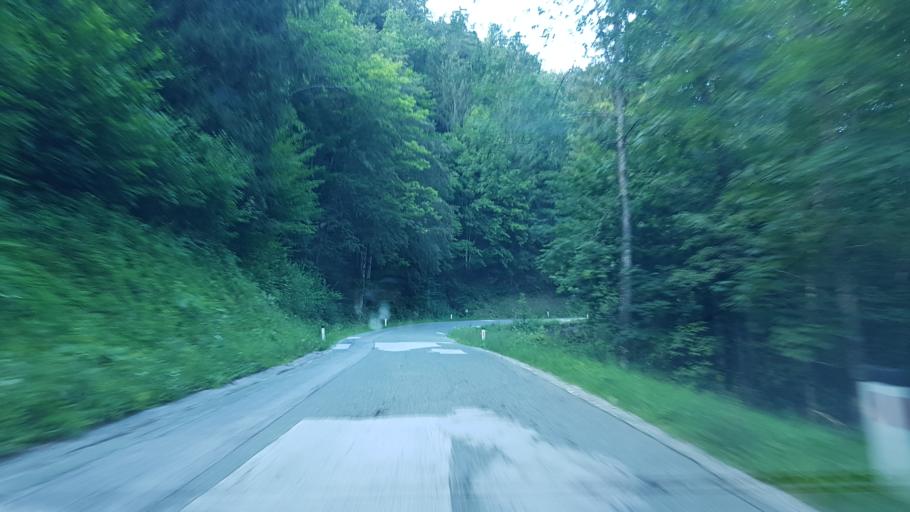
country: SI
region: Ziri
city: Ziri
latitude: 46.0844
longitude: 14.0822
